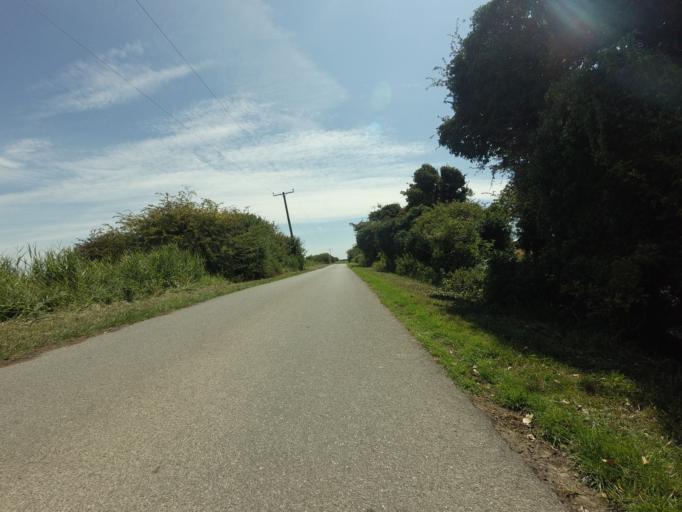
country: GB
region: England
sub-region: Kent
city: Lydd
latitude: 50.9803
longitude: 0.8456
